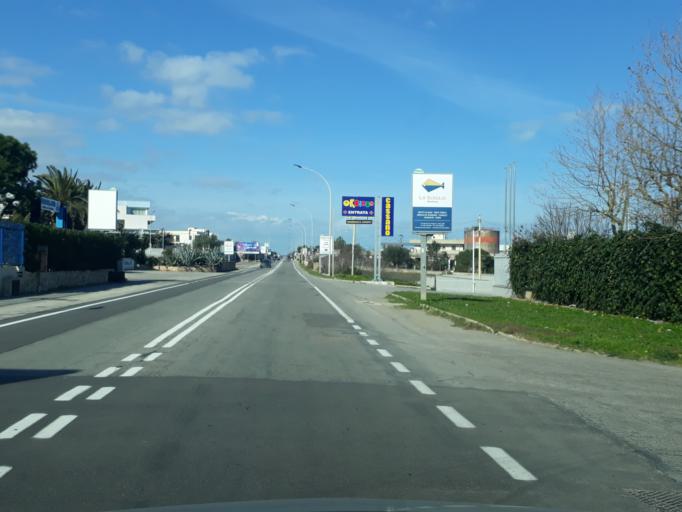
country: IT
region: Apulia
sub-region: Provincia di Bari
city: Monopoli
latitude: 40.9688
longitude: 17.2683
